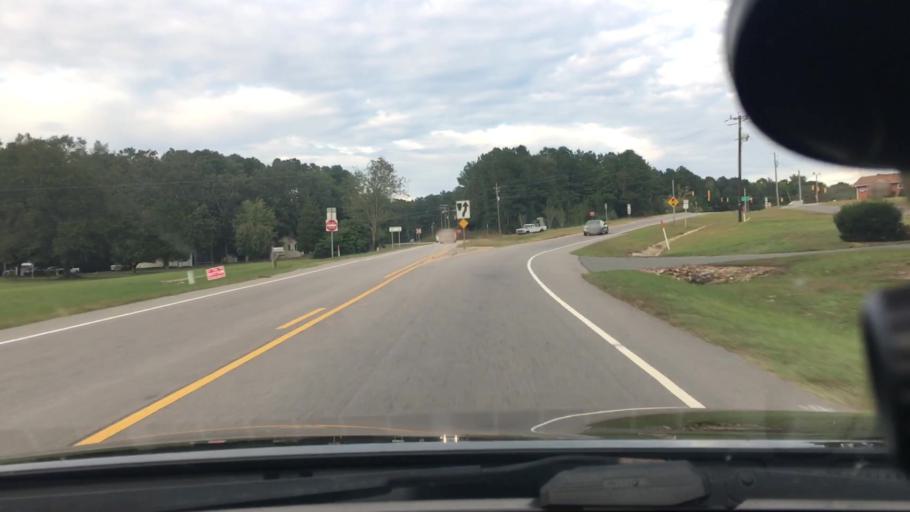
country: US
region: North Carolina
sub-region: Lee County
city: Sanford
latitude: 35.4028
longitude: -79.2340
